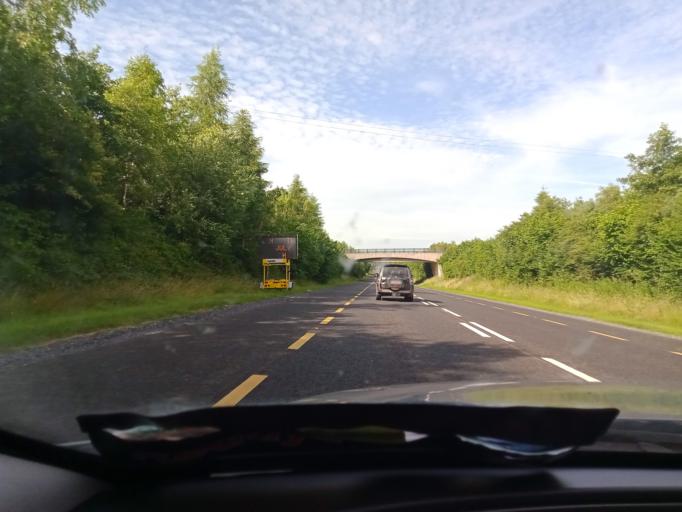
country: IE
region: Leinster
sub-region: An Iarmhi
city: An Muileann gCearr
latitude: 53.4921
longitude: -7.3344
